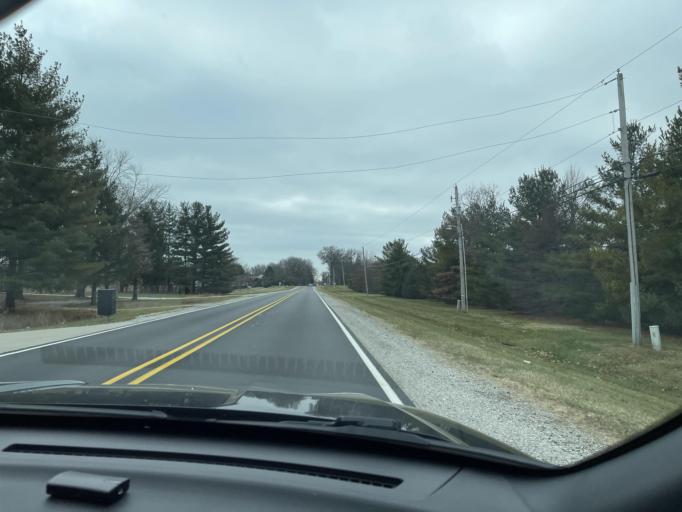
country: US
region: Illinois
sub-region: Sangamon County
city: Leland Grove
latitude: 39.7966
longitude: -89.7392
